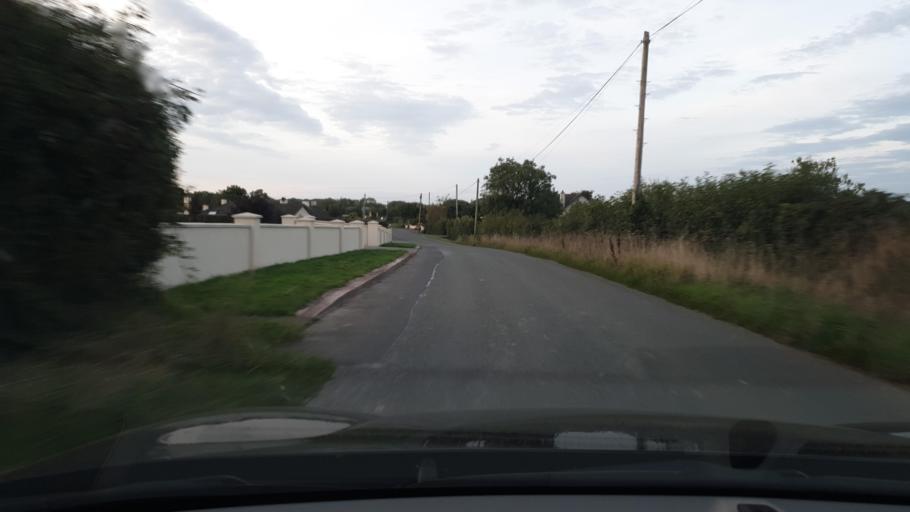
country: IE
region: Leinster
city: Balrothery
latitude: 53.5633
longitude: -6.1654
